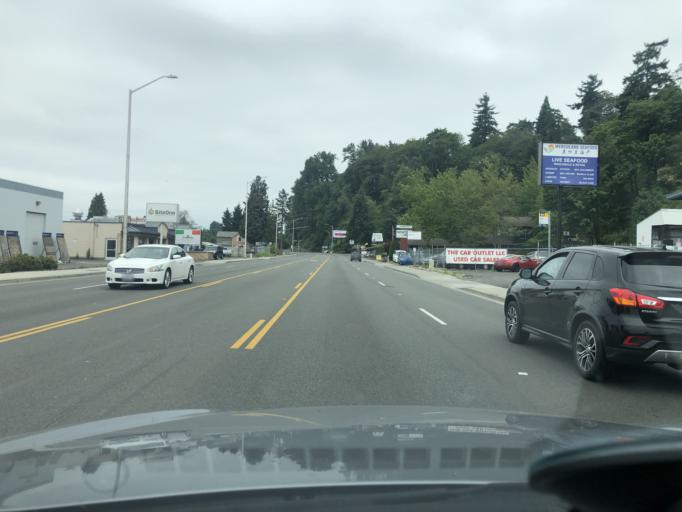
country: US
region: Washington
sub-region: King County
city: Kent
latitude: 47.3752
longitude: -122.2302
